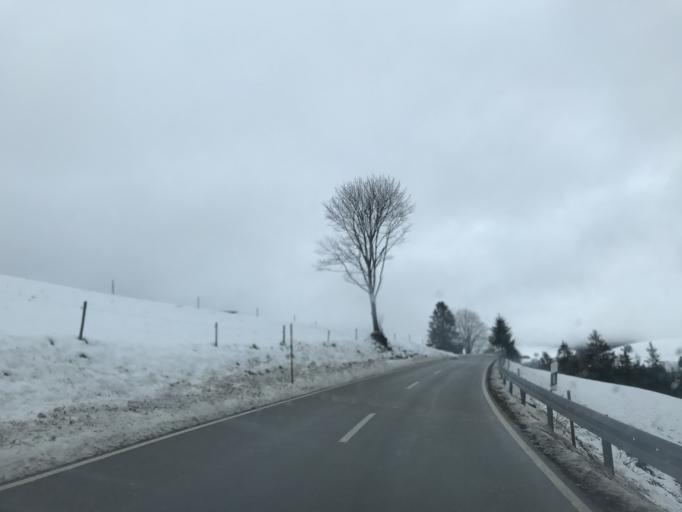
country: DE
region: Baden-Wuerttemberg
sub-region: Freiburg Region
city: Hasel
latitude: 47.6922
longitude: 7.8992
